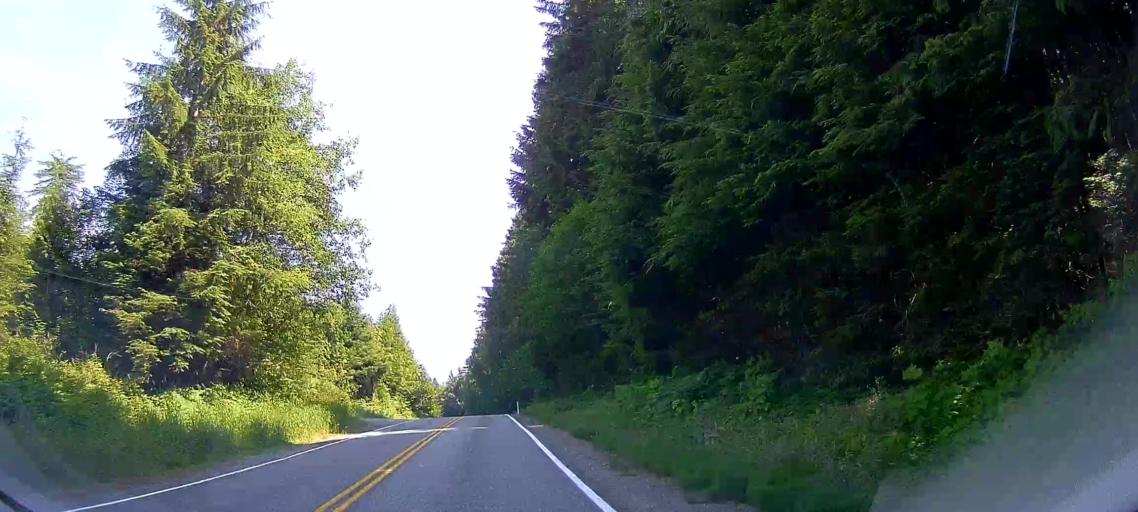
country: US
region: Washington
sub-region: Snohomish County
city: Arlington Heights
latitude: 48.3386
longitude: -122.0494
